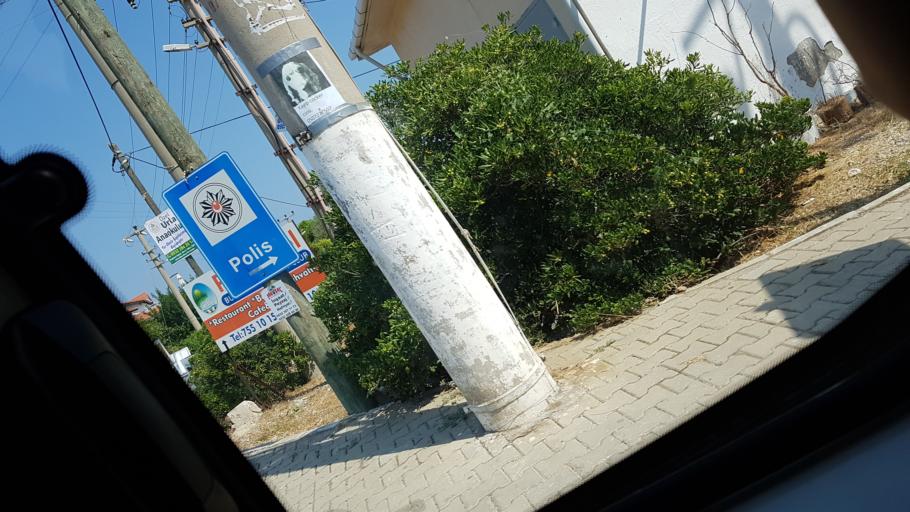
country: TR
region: Izmir
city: Urla
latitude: 38.3945
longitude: 26.7423
